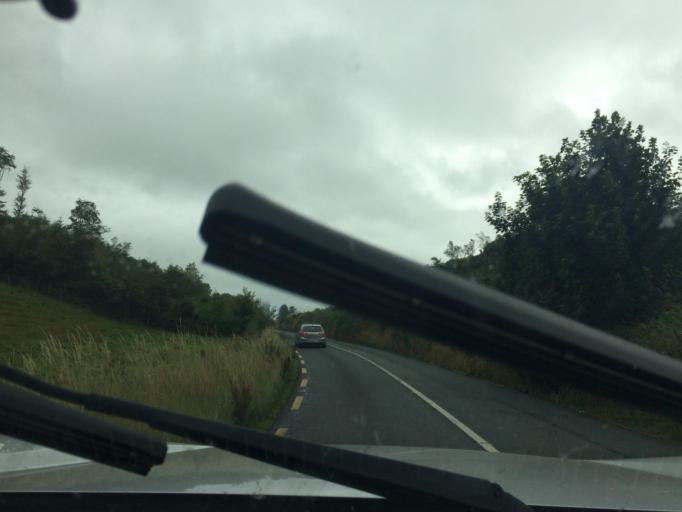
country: IE
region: Munster
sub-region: South Tipperary
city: Cluain Meala
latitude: 52.2391
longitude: -7.7223
